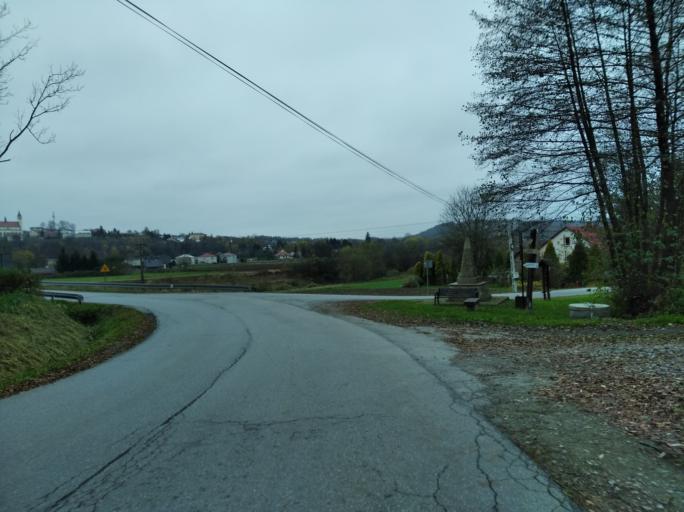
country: PL
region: Subcarpathian Voivodeship
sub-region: Powiat strzyzowski
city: Frysztak
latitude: 49.8381
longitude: 21.6217
